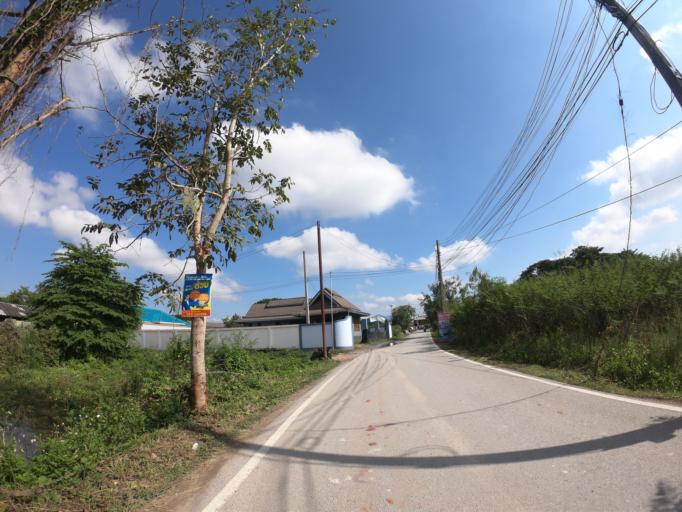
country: TH
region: Chiang Mai
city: San Sai
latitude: 18.8471
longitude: 99.0507
